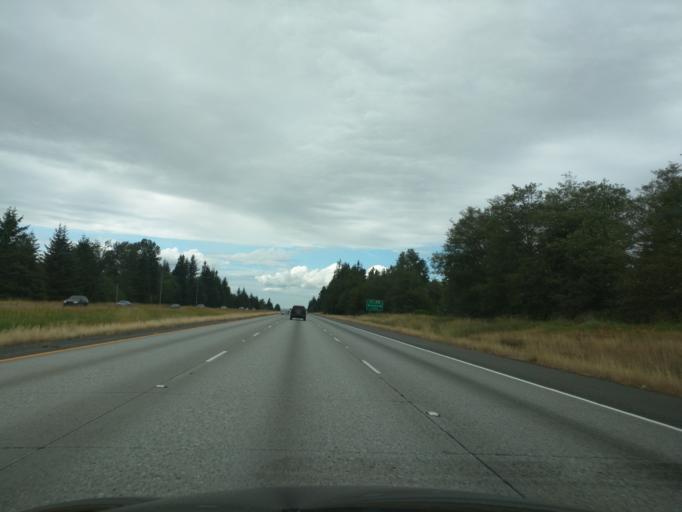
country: US
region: Washington
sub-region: Snohomish County
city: Stanwood
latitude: 48.2920
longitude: -122.2969
